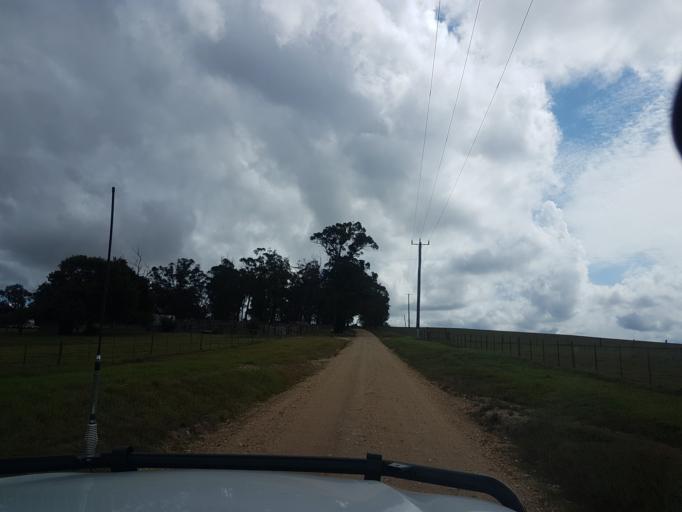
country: AU
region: Victoria
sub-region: East Gippsland
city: Bairnsdale
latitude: -37.7846
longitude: 147.5389
